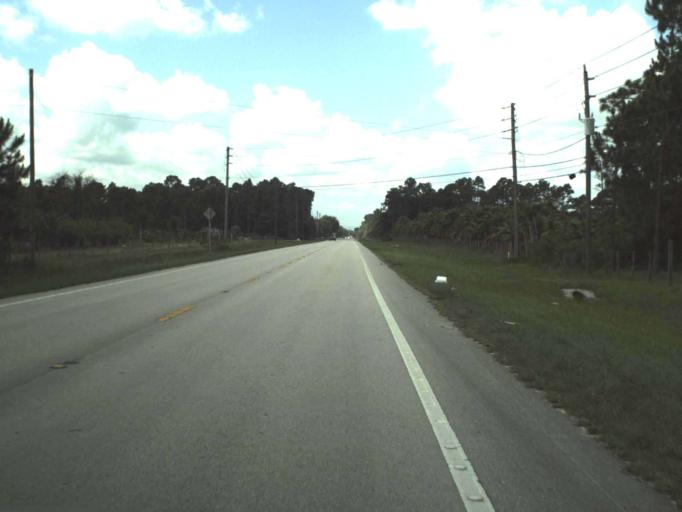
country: US
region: Florida
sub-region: Volusia County
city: Samsula-Spruce Creek
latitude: 28.9460
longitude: -81.1005
